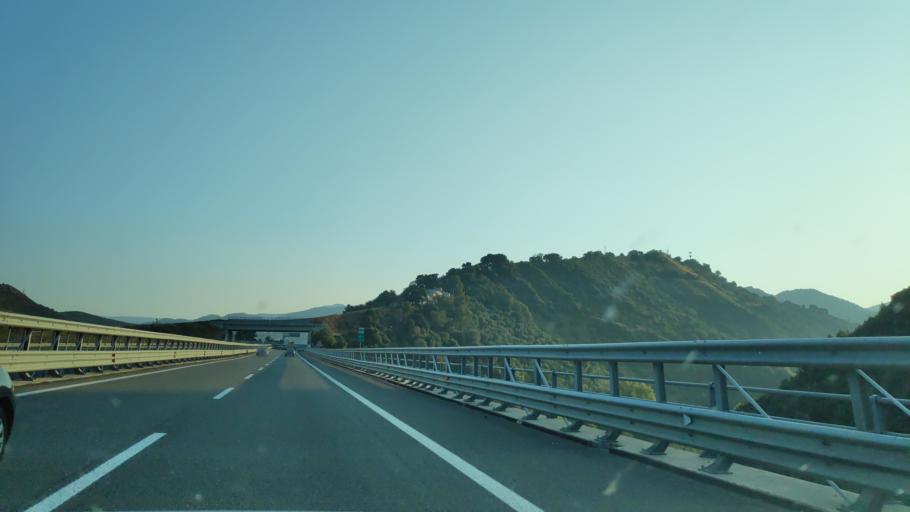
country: IT
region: Calabria
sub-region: Provincia di Catanzaro
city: Nocera Scalo
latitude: 39.0346
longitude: 16.1351
